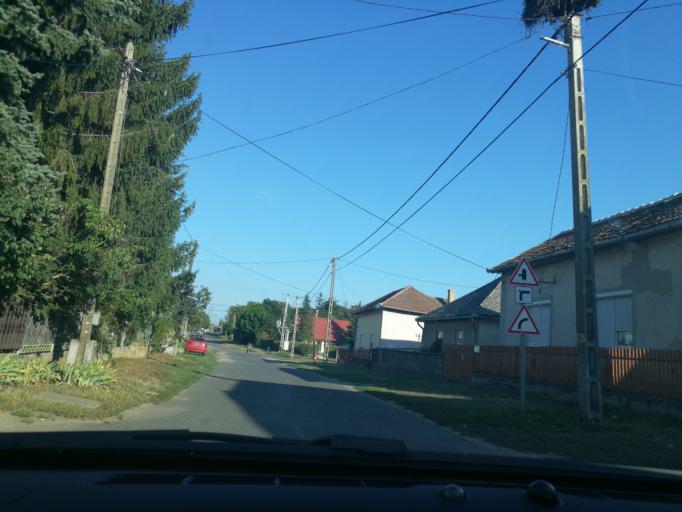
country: HU
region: Szabolcs-Szatmar-Bereg
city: Tiszabercel
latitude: 48.1645
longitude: 21.5912
